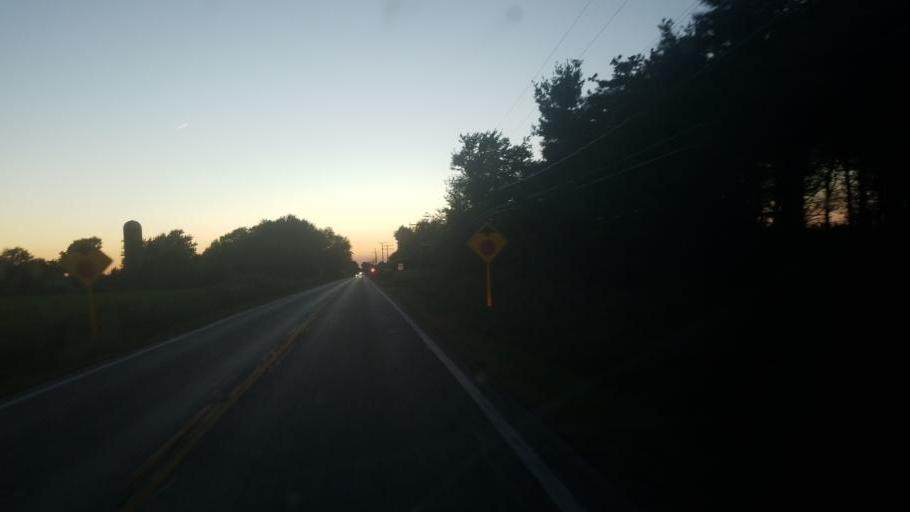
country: US
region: Ohio
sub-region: Ashtabula County
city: Jefferson
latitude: 41.7517
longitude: -80.6640
